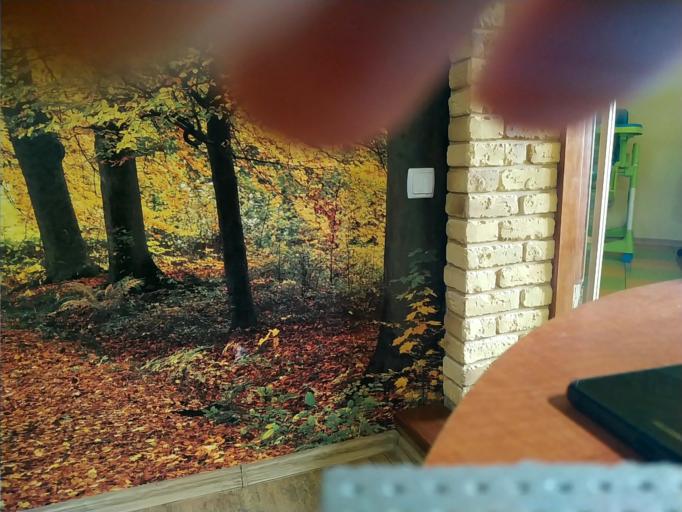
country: RU
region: Tverskaya
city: Likhoslavl'
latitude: 56.9813
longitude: 35.3274
